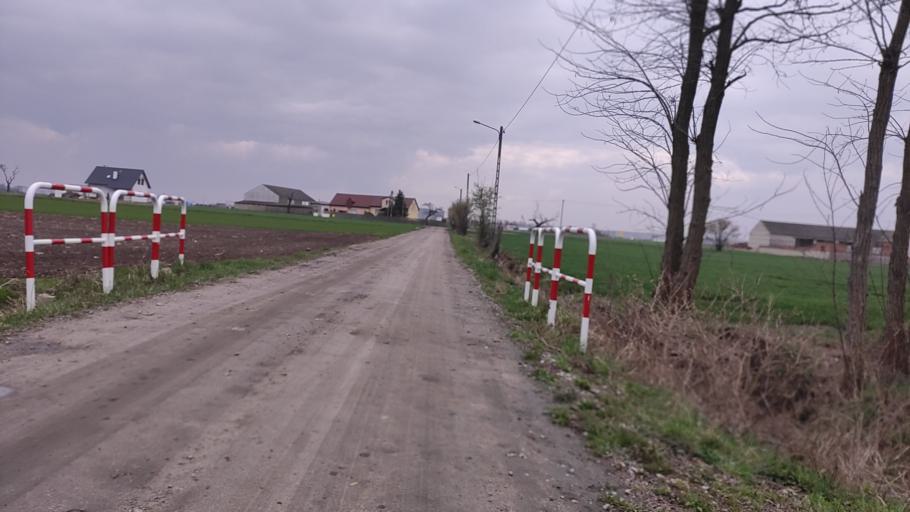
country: PL
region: Greater Poland Voivodeship
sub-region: Powiat poznanski
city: Swarzedz
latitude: 52.4078
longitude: 17.1389
